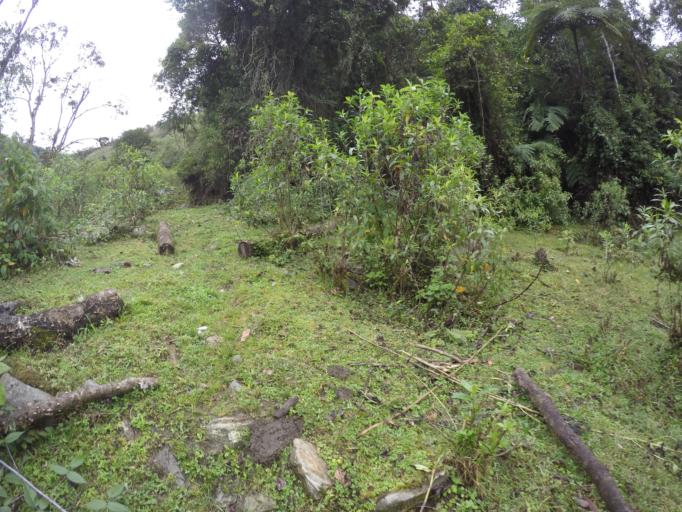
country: CO
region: Tolima
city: Cajamarca
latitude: 4.5257
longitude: -75.3607
